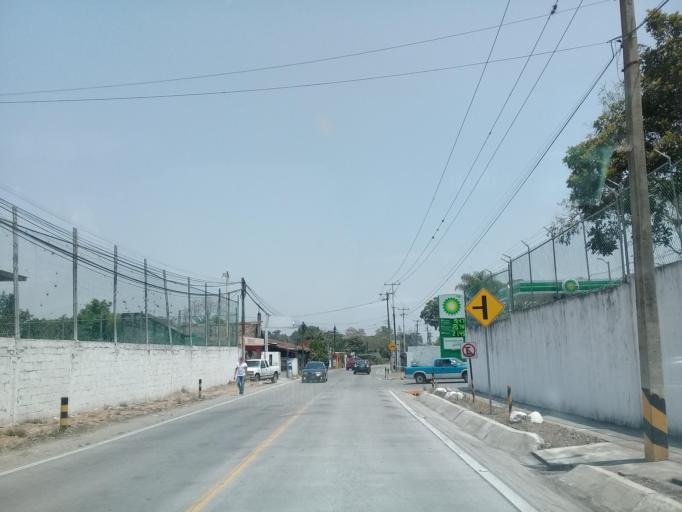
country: MX
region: Veracruz
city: Paraje Nuevo
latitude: 18.8734
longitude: -96.8665
